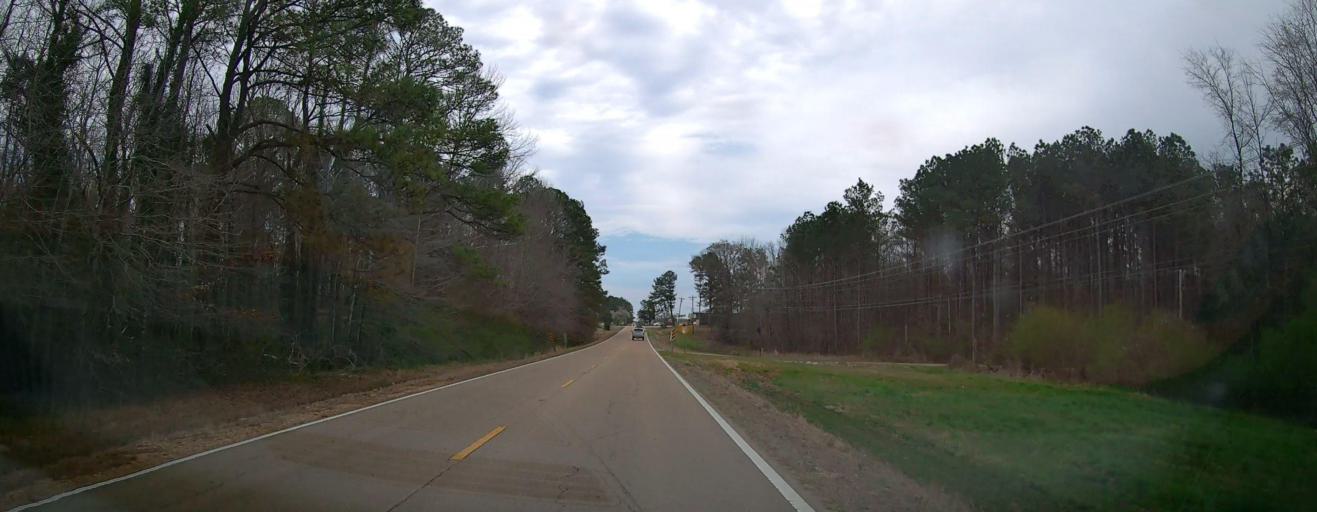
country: US
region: Mississippi
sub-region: Itawamba County
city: Fulton
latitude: 34.2380
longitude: -88.2685
